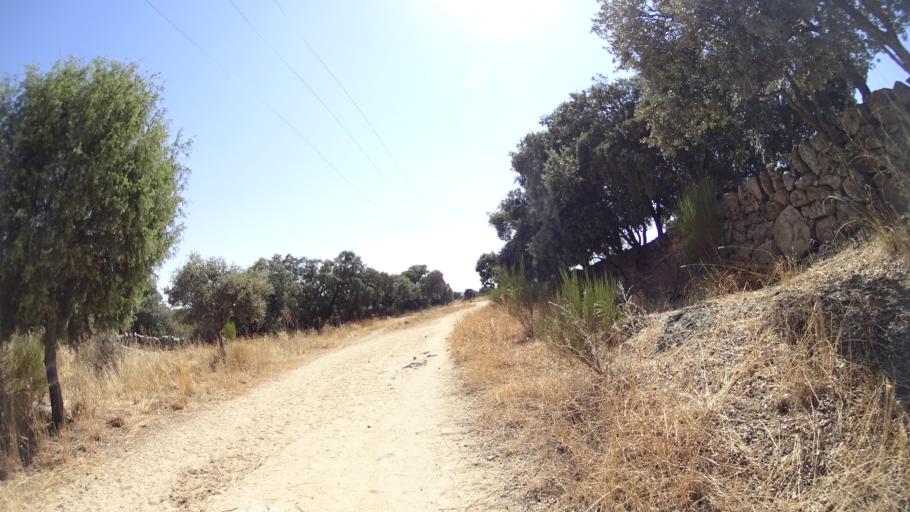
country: ES
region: Madrid
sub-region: Provincia de Madrid
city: Galapagar
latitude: 40.6030
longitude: -4.0100
